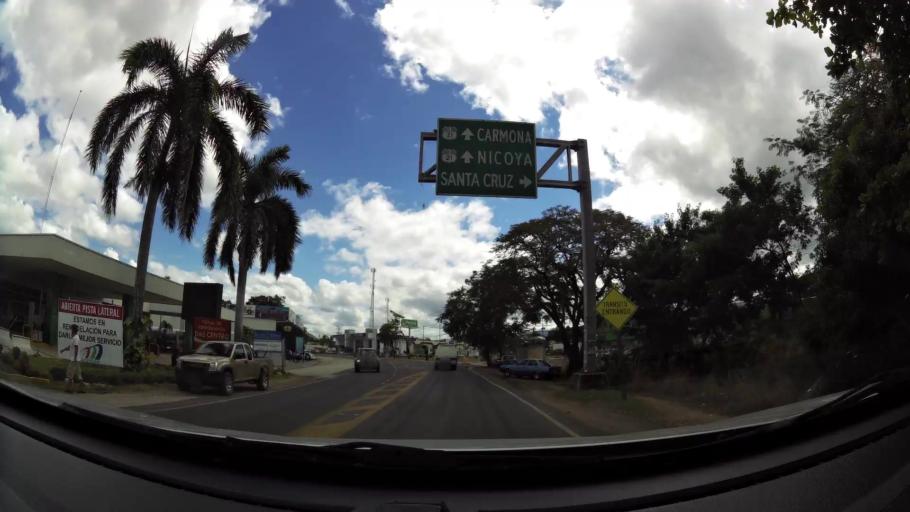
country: CR
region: Guanacaste
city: Santa Cruz
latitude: 10.2685
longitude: -85.5883
